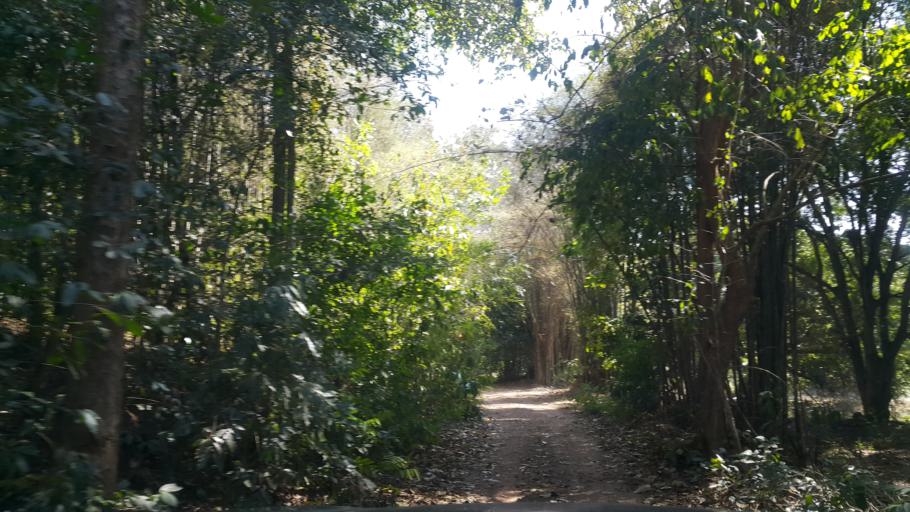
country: TH
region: Sukhothai
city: Thung Saliam
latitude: 17.3431
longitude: 99.5838
